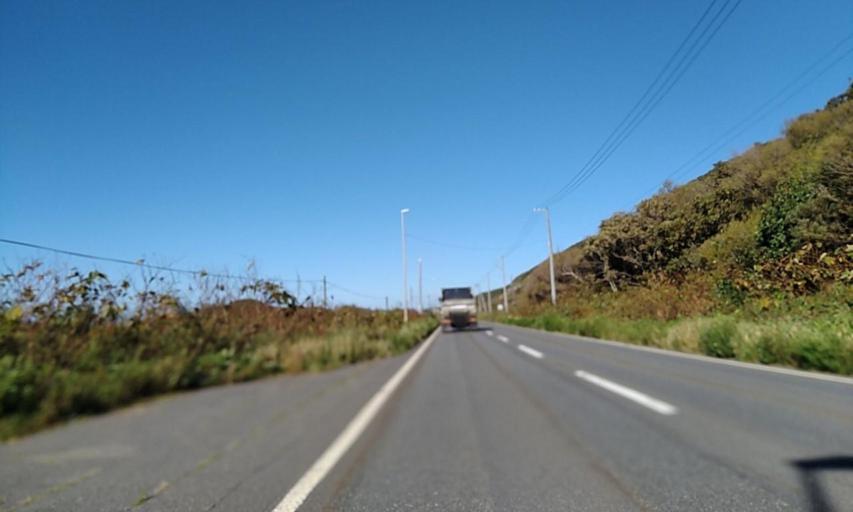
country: JP
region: Hokkaido
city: Shizunai-furukawacho
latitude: 42.4659
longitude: 142.1471
